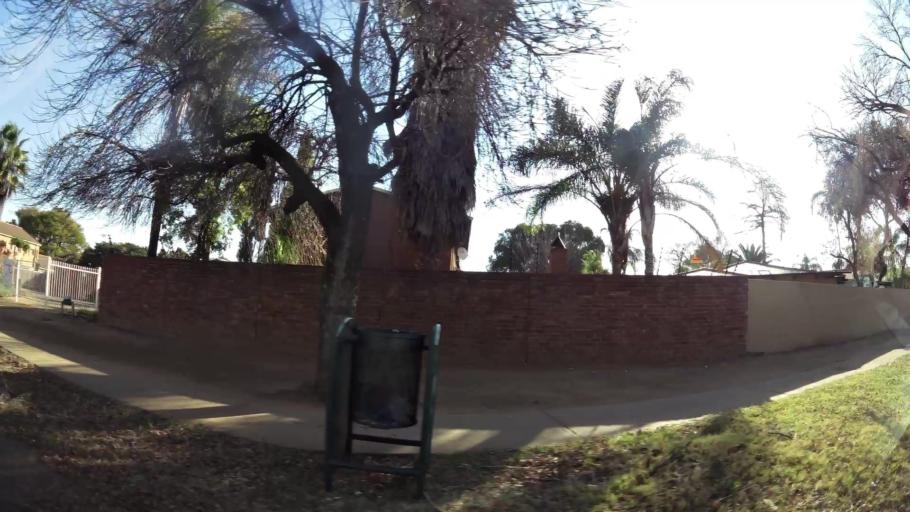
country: ZA
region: Gauteng
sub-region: City of Tshwane Metropolitan Municipality
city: Pretoria
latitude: -25.7070
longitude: 28.2428
